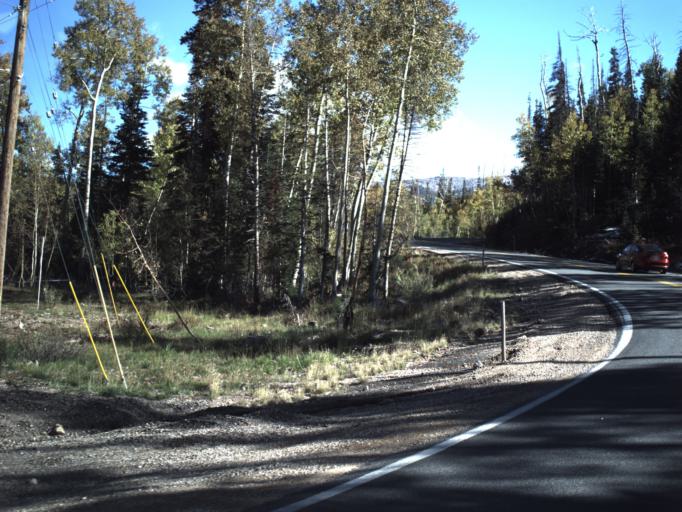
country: US
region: Utah
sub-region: Iron County
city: Parowan
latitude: 37.7094
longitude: -112.8518
